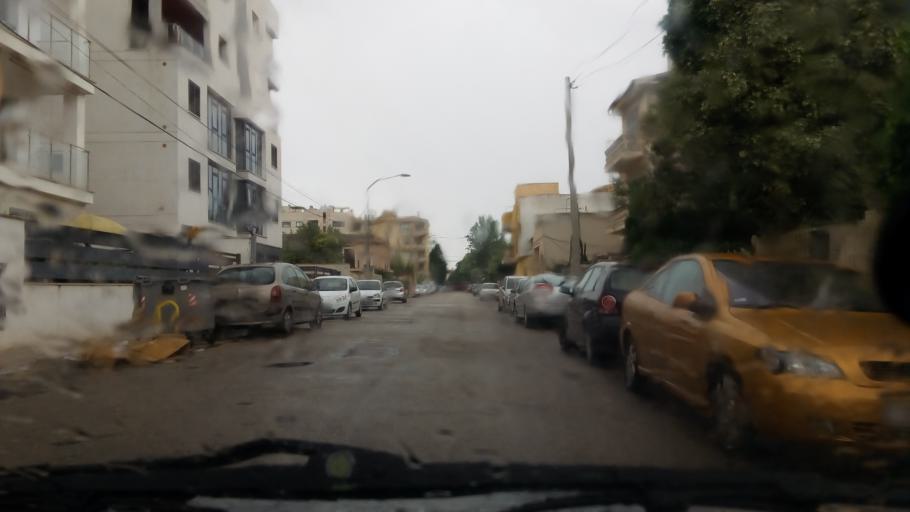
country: ES
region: Balearic Islands
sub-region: Illes Balears
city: Manacor
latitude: 39.5674
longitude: 3.2190
